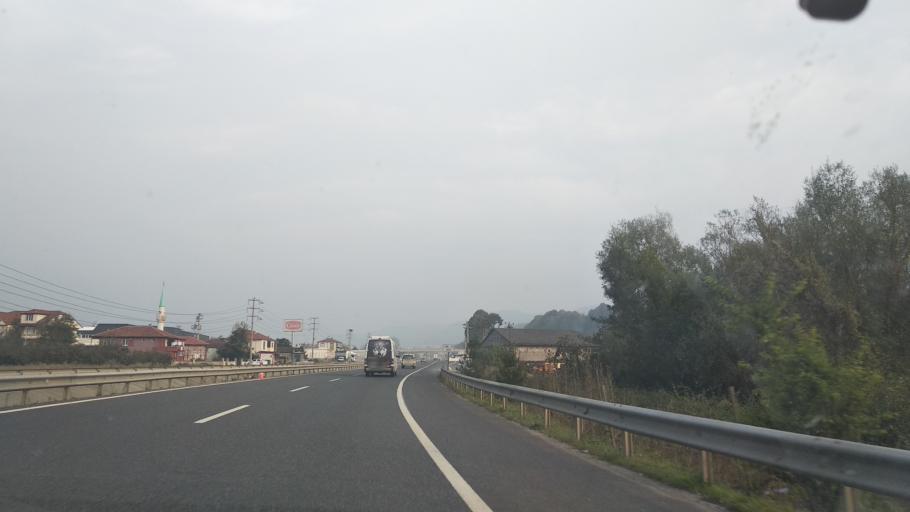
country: TR
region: Duzce
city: Kaynasli
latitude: 40.7838
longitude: 31.2717
